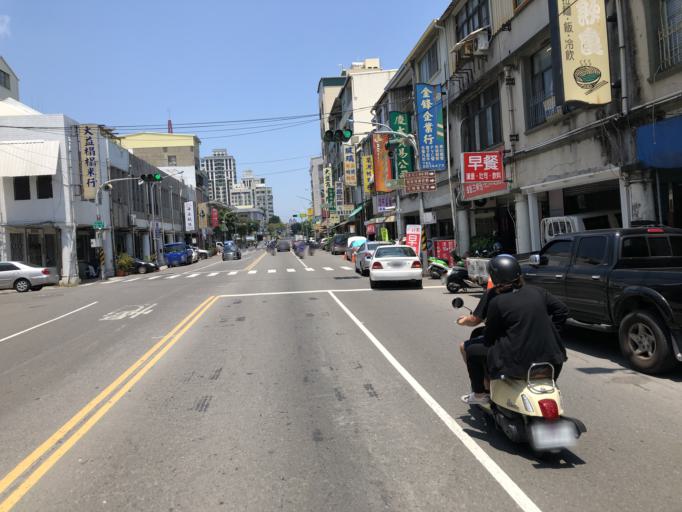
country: TW
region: Kaohsiung
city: Kaohsiung
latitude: 22.6255
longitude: 120.2775
